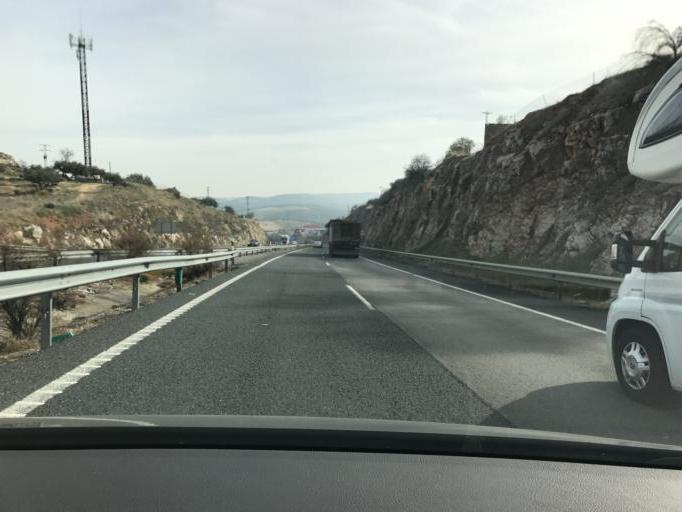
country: ES
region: Andalusia
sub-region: Provincia de Granada
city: Loja
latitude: 37.1605
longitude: -4.1377
